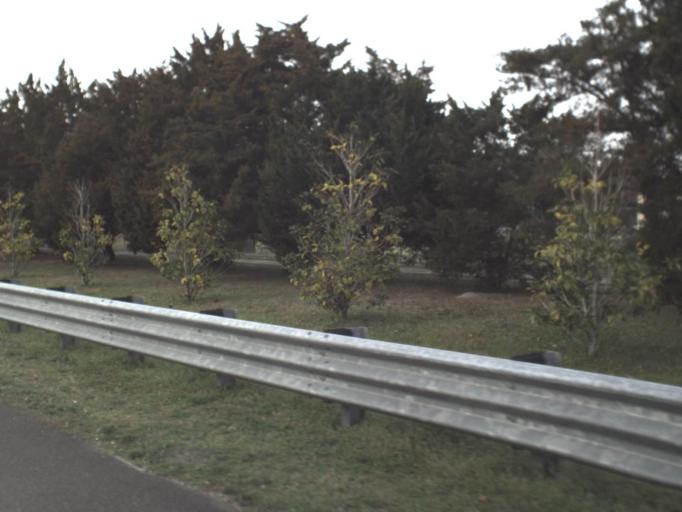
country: US
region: Florida
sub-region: Bay County
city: Tyndall Air Force Base
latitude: 30.0743
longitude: -85.5955
